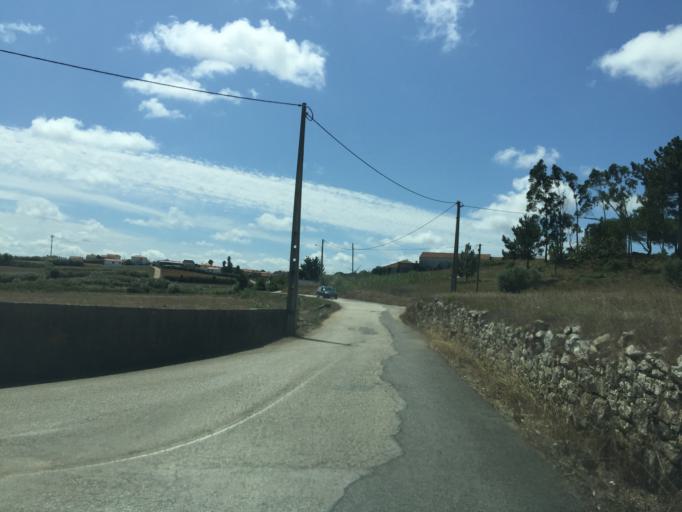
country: PT
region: Leiria
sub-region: Bombarral
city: Bombarral
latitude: 39.2860
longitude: -9.2246
